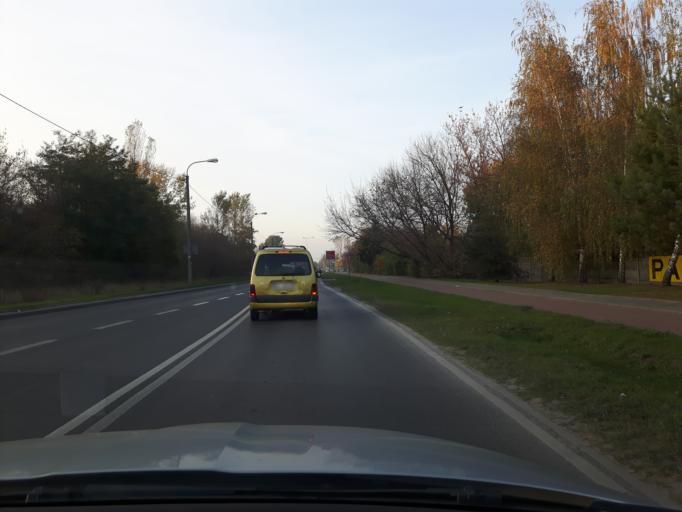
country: PL
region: Masovian Voivodeship
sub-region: Warszawa
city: Praga Poludnie
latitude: 52.2662
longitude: 21.0748
